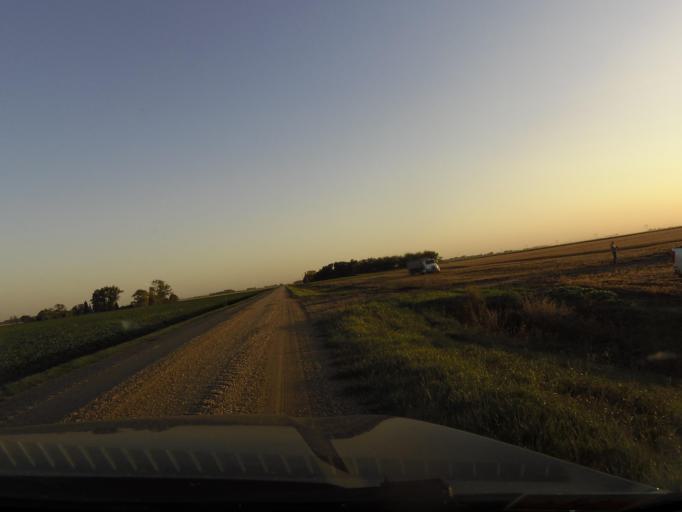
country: US
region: North Dakota
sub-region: Walsh County
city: Grafton
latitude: 48.3865
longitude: -97.2555
